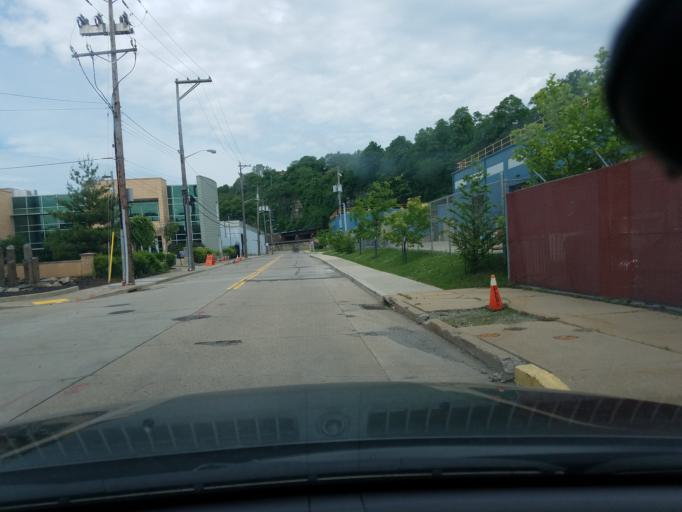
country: US
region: Pennsylvania
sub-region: Allegheny County
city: Bellevue
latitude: 40.4720
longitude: -80.0400
